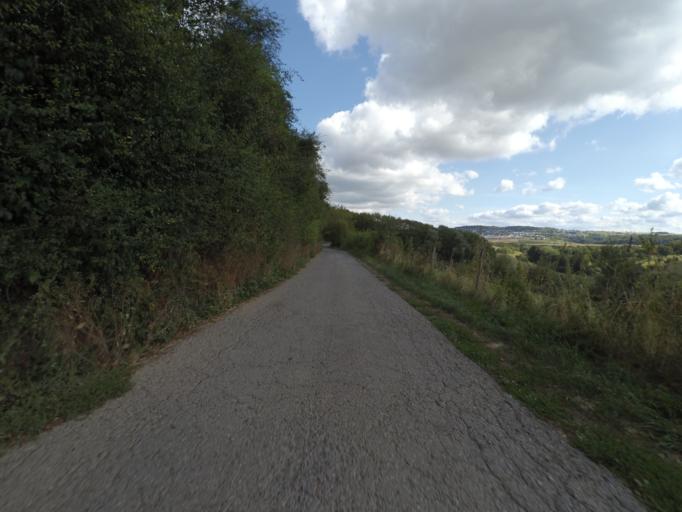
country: DE
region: Rheinland-Pfalz
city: Kirf
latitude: 49.5303
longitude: 6.5011
